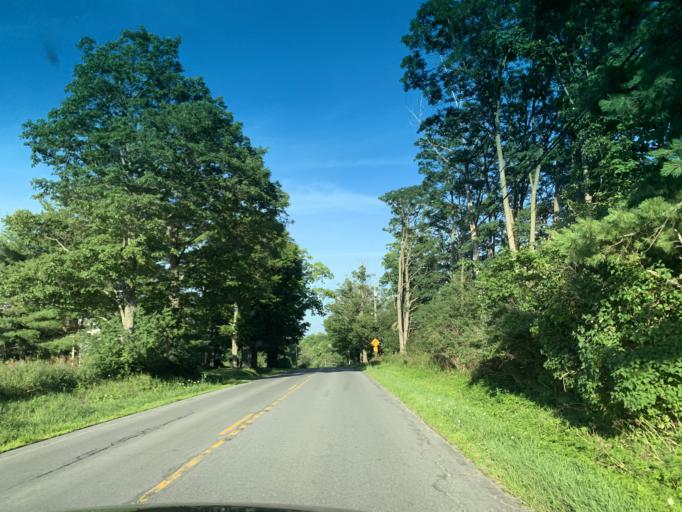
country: US
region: New York
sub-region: Oneida County
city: Clinton
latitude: 43.0551
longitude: -75.4380
